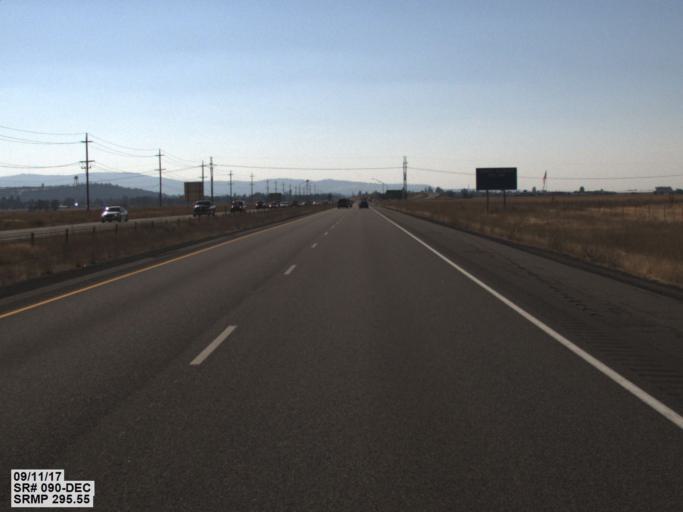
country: US
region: Washington
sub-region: Spokane County
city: Liberty Lake
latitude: 47.6680
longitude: -117.1202
